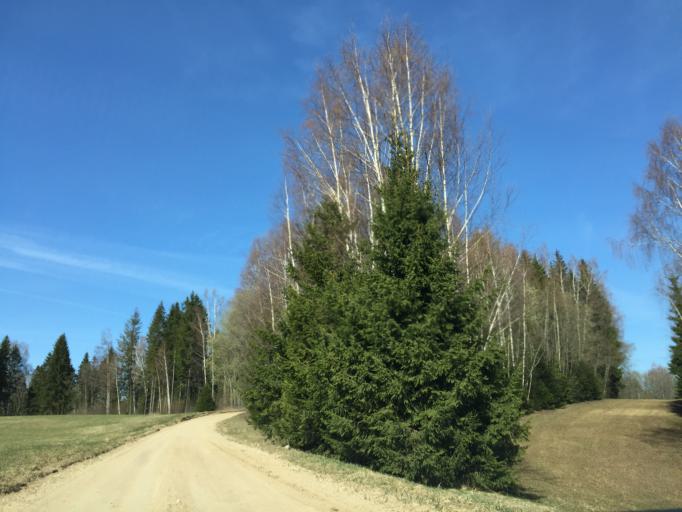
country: EE
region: Vorumaa
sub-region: Antsla vald
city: Vana-Antsla
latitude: 57.9789
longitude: 26.3536
